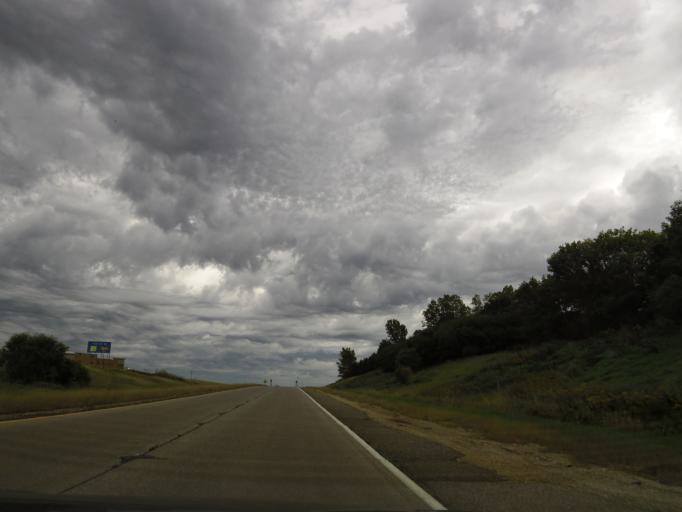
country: US
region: Minnesota
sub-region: Dakota County
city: Burnsville
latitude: 44.7438
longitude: -93.2754
